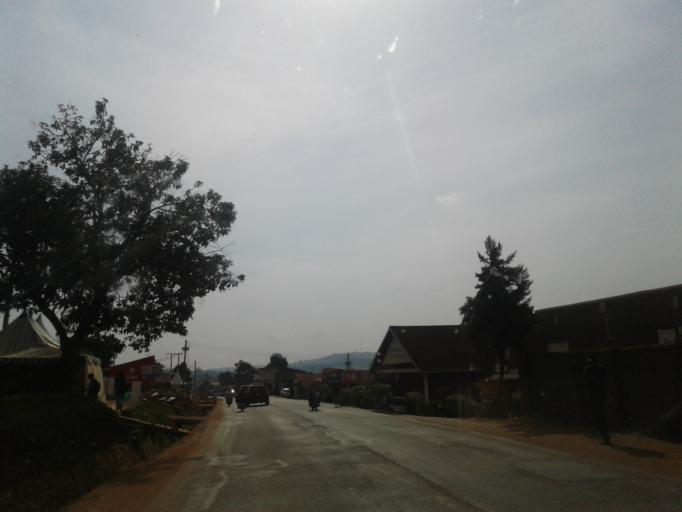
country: UG
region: Central Region
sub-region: Wakiso District
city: Kireka
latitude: 0.3415
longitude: 32.6418
